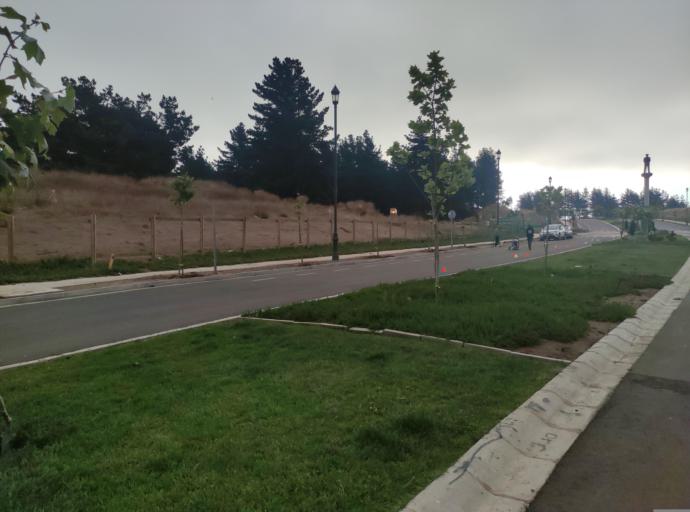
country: CL
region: Valparaiso
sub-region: Provincia de Valparaiso
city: Vina del Mar
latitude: -32.9444
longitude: -71.5277
